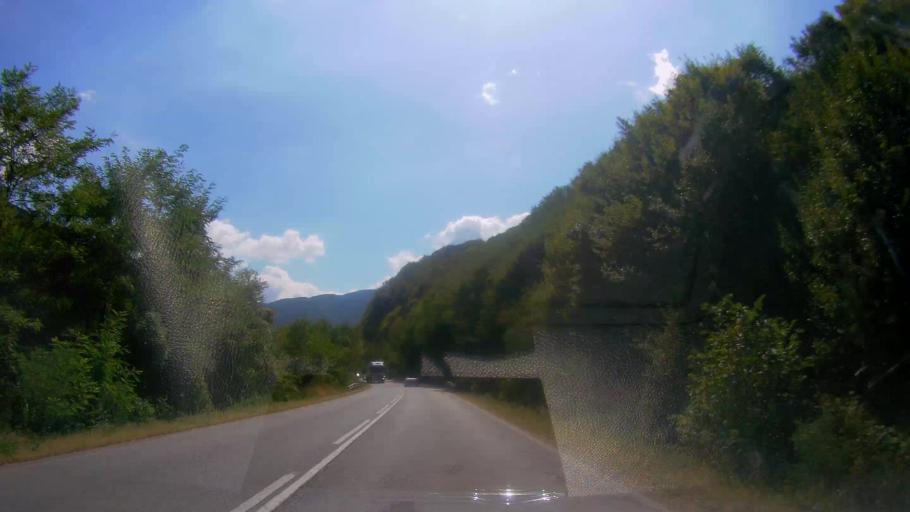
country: BG
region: Stara Zagora
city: Gurkovo
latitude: 42.7261
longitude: 25.7125
